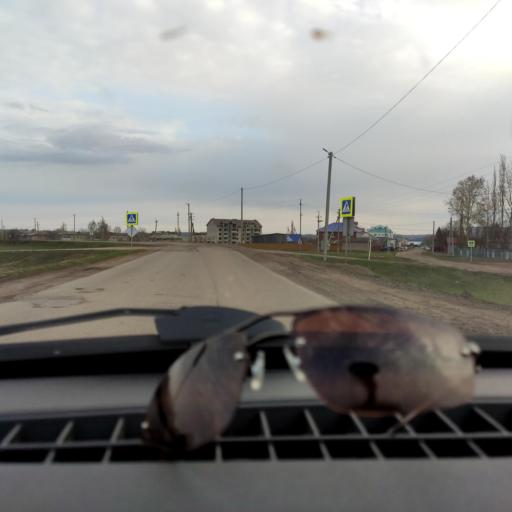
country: RU
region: Bashkortostan
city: Kabakovo
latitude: 54.5275
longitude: 56.1573
